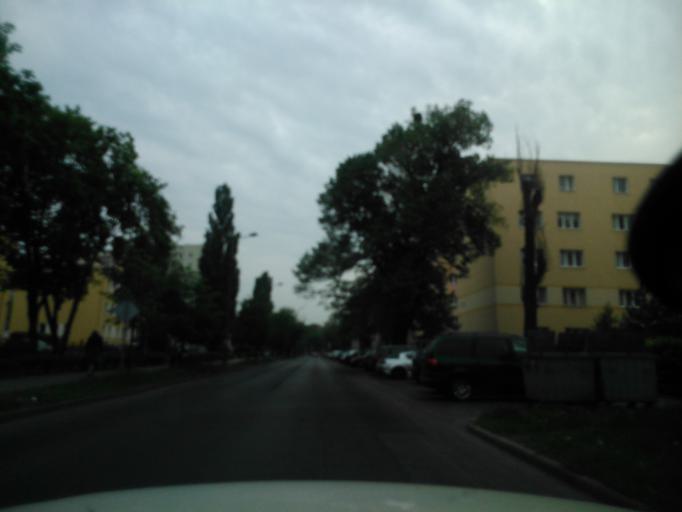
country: PL
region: Kujawsko-Pomorskie
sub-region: Torun
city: Torun
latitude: 53.0192
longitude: 18.6092
